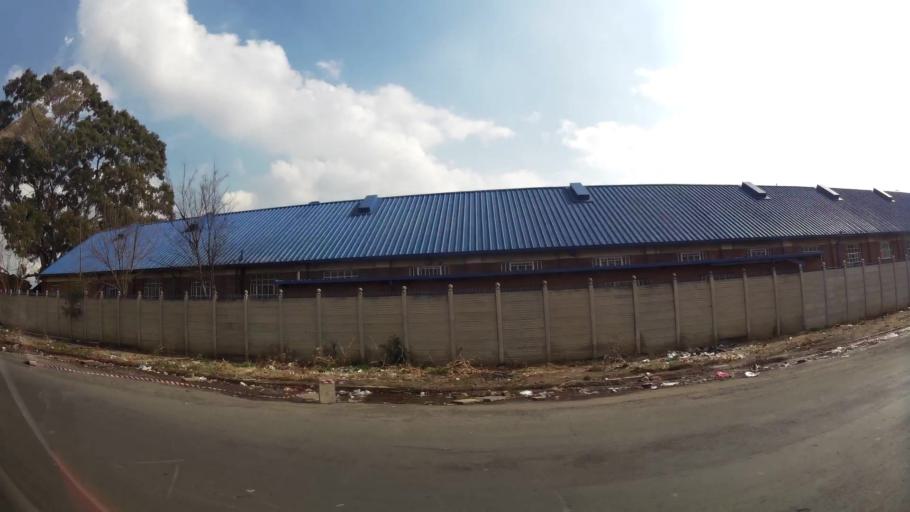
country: ZA
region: Gauteng
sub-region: Sedibeng District Municipality
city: Vereeniging
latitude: -26.6790
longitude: 27.9329
